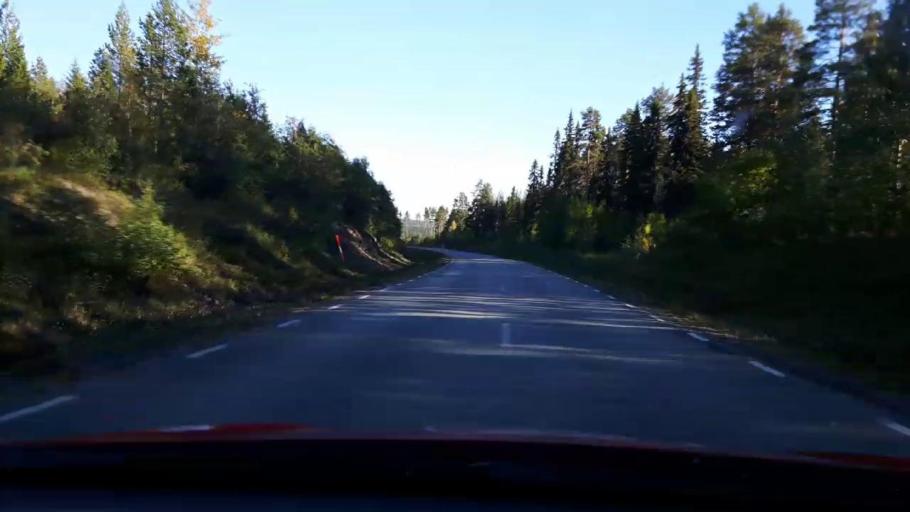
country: SE
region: Jaemtland
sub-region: OEstersunds Kommun
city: Lit
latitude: 63.7507
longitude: 14.7164
